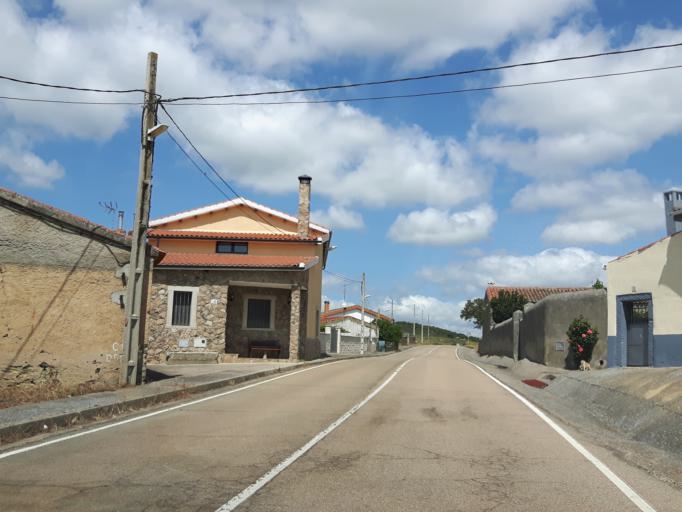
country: ES
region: Castille and Leon
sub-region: Provincia de Salamanca
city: Castillejo de Martin Viejo
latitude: 40.7035
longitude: -6.6717
